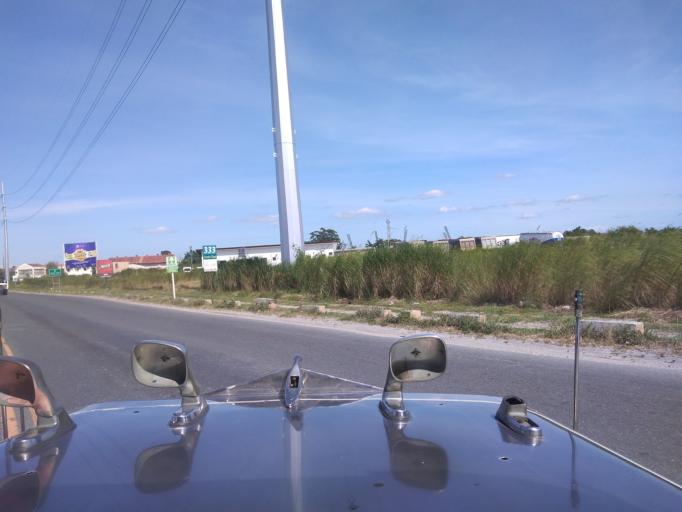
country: PH
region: Central Luzon
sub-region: Province of Pampanga
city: San Juan
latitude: 15.0207
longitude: 120.6683
